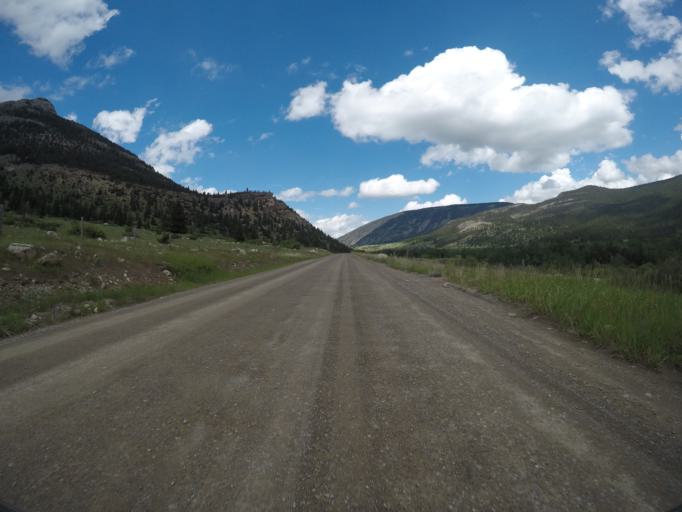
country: US
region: Montana
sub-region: Park County
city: Livingston
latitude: 45.5275
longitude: -110.2186
